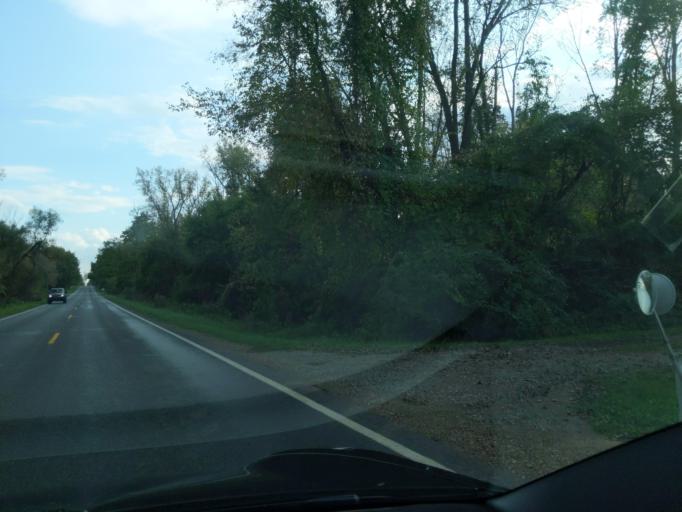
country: US
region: Michigan
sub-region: Jackson County
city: Jackson
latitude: 42.3155
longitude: -84.4627
